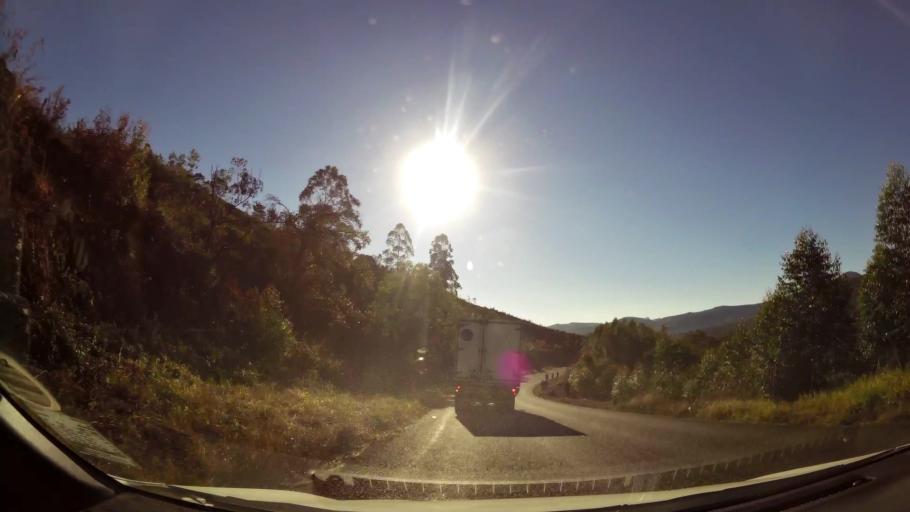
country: ZA
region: Limpopo
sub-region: Mopani District Municipality
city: Tzaneen
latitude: -23.9384
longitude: 30.0224
